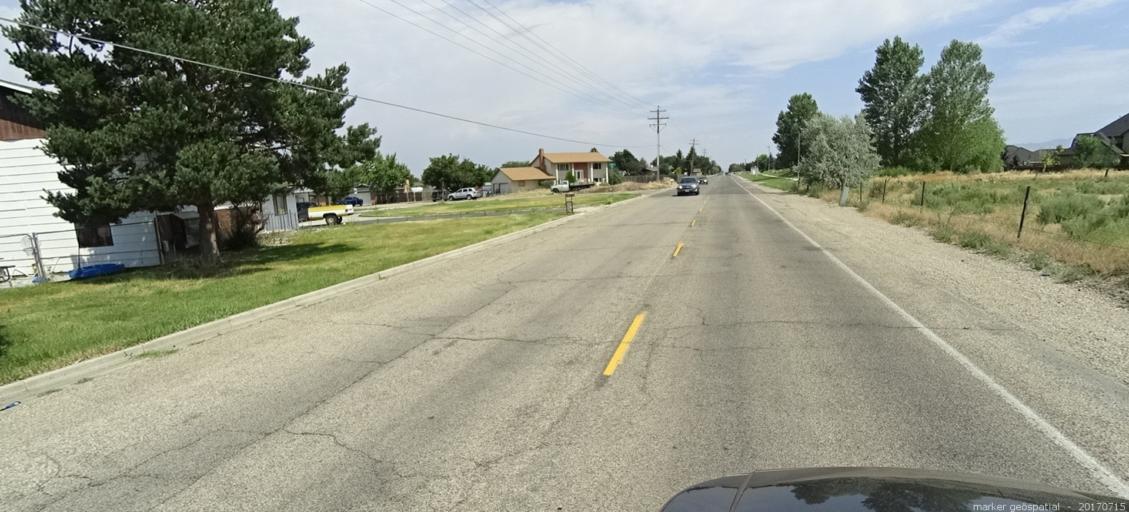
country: US
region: Idaho
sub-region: Ada County
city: Garden City
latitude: 43.5459
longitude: -116.2742
